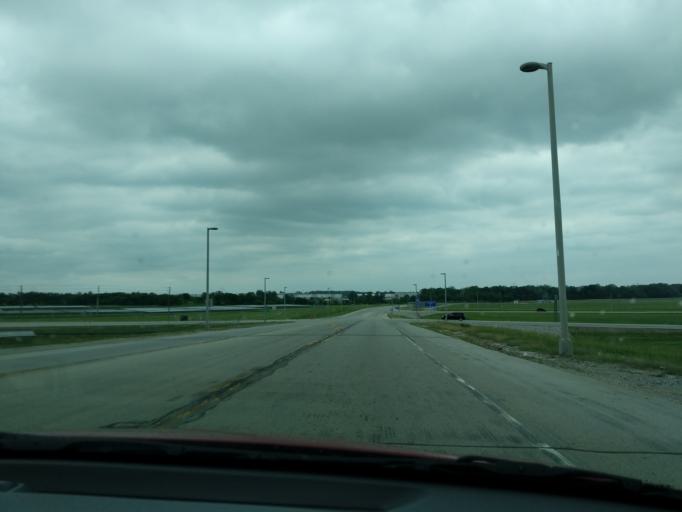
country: US
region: Indiana
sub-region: Hendricks County
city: Plainfield
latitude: 39.7005
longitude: -86.3188
